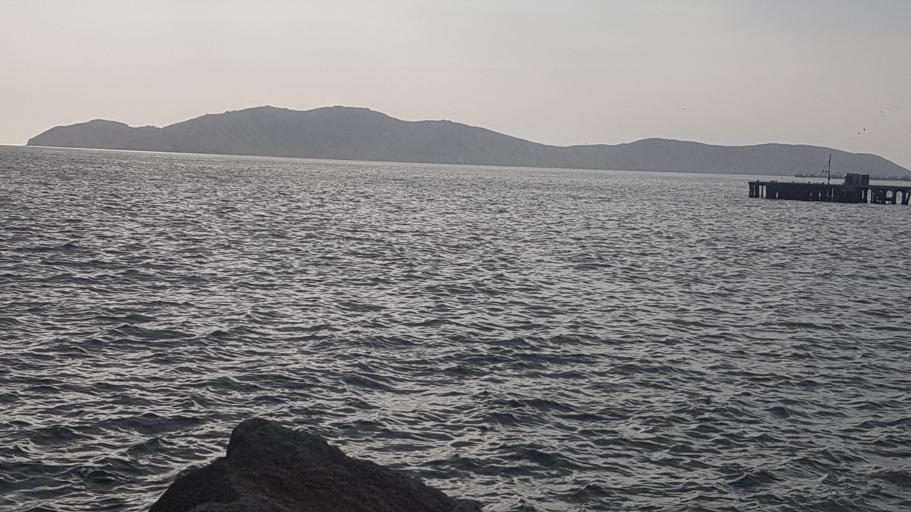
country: PE
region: Ancash
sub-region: Provincia de Santa
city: Chimbote
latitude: -9.0945
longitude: -78.5736
